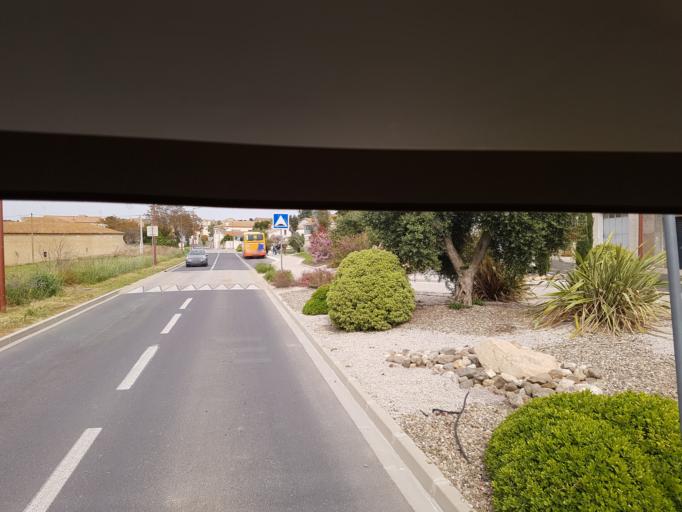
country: FR
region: Languedoc-Roussillon
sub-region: Departement de l'Herault
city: Lespignan
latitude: 43.2699
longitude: 3.1689
